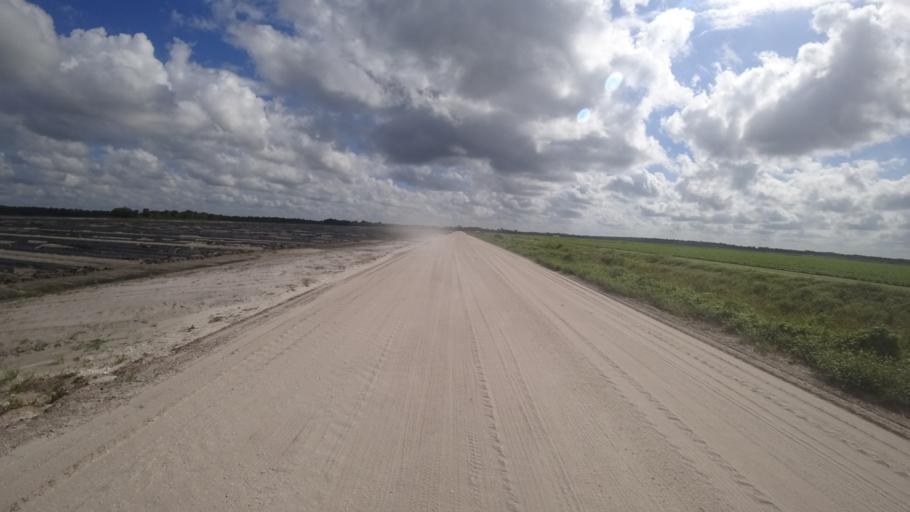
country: US
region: Florida
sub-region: Sarasota County
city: Lake Sarasota
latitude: 27.4132
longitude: -82.2099
